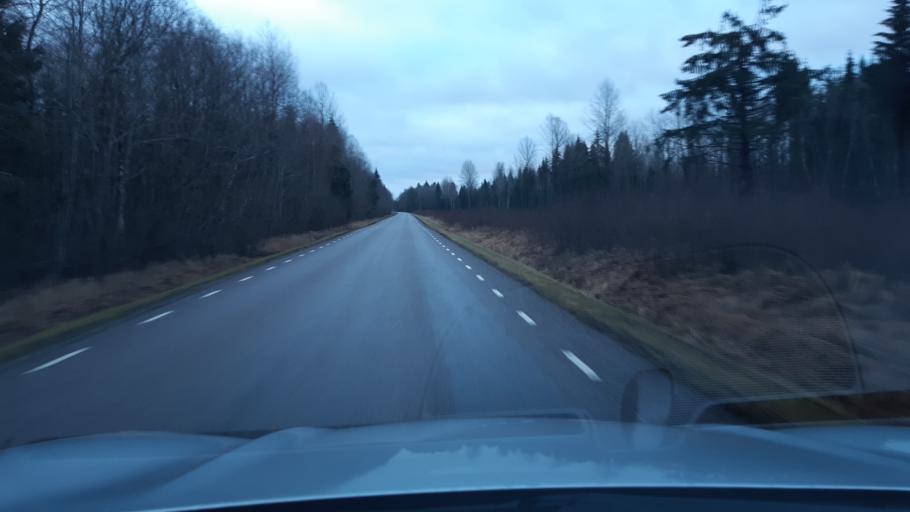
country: EE
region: Raplamaa
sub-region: Kohila vald
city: Kohila
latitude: 59.1358
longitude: 24.6602
